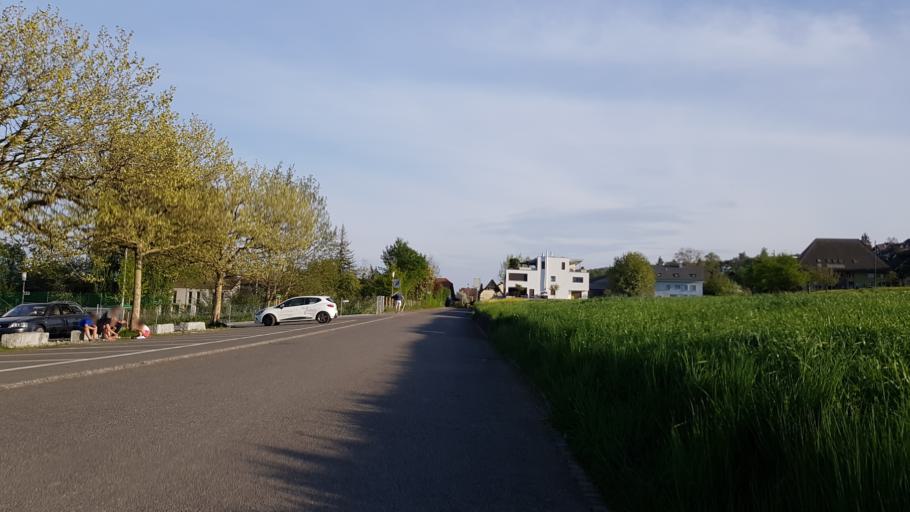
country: CH
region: Aargau
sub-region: Bezirk Kulm
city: Reinach
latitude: 47.2703
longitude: 8.2086
